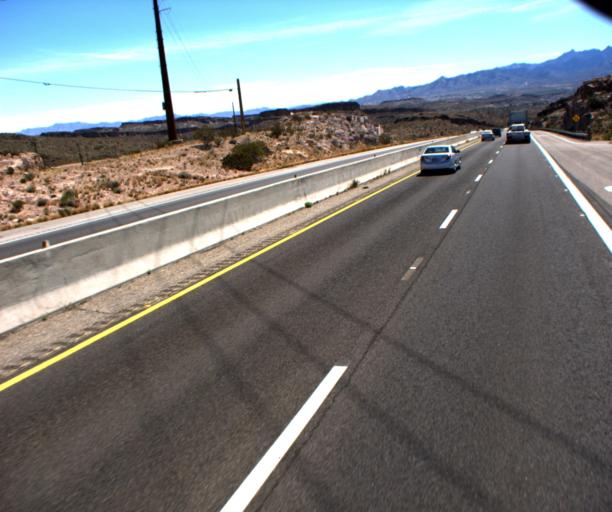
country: US
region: Arizona
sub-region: Mohave County
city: Kingman
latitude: 35.2061
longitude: -114.0954
